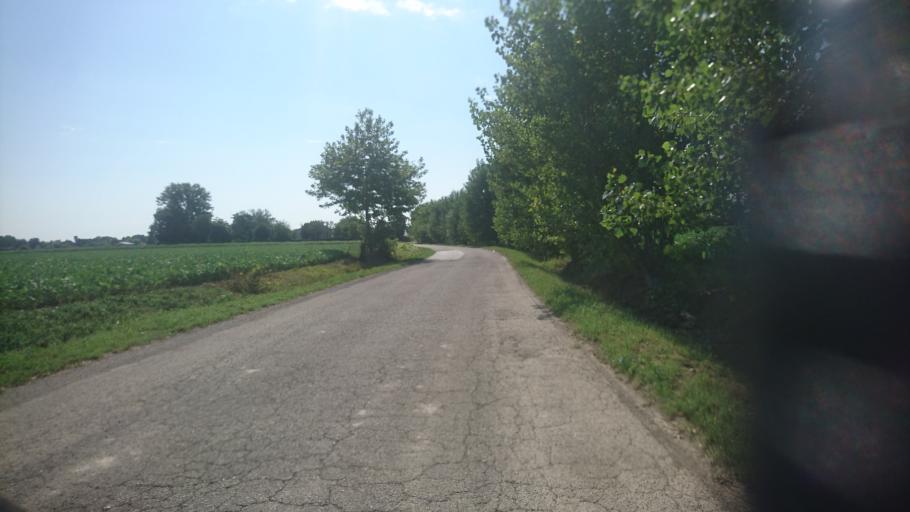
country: IT
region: Veneto
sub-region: Provincia di Padova
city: Mandriola-Sant'Agostino
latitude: 45.3774
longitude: 11.8324
